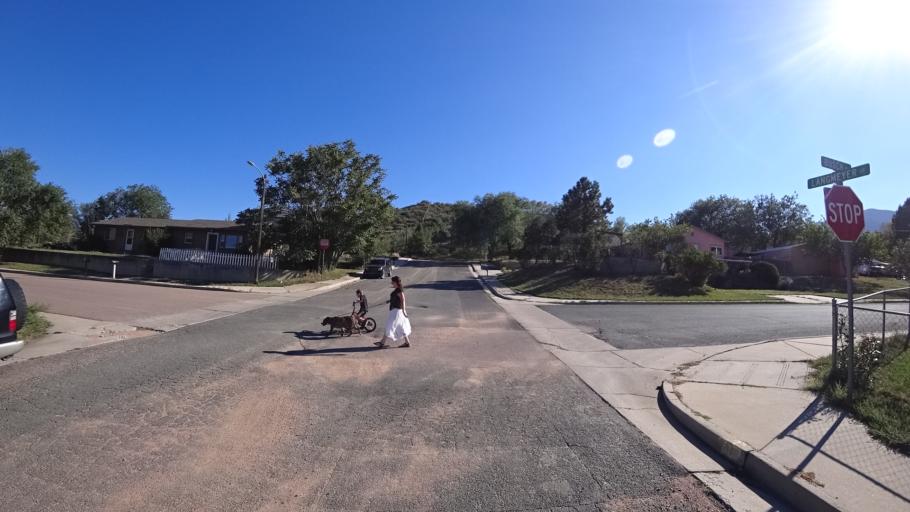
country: US
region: Colorado
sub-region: El Paso County
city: Colorado Springs
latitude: 38.8344
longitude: -104.8704
